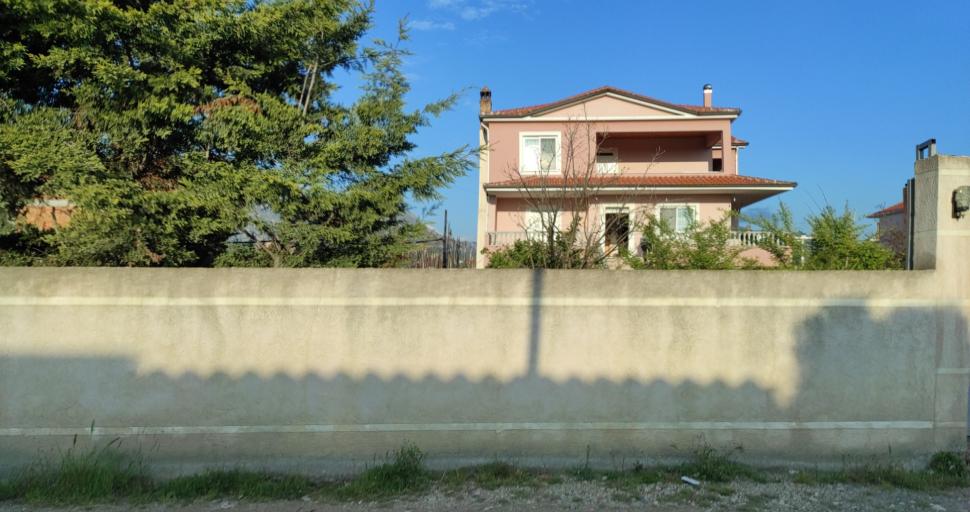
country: AL
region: Durres
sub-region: Rrethi i Krujes
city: Fushe-Kruje
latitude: 41.4791
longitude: 19.7347
